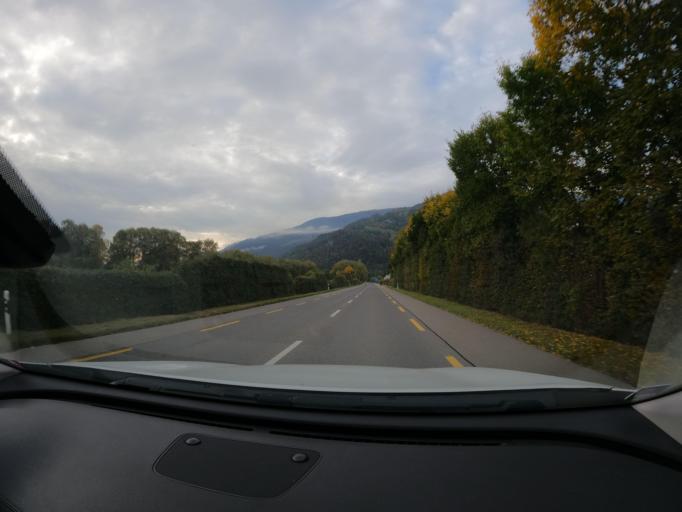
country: CH
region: Bern
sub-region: Interlaken-Oberhasli District
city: Unterseen
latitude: 46.6771
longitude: 7.8296
